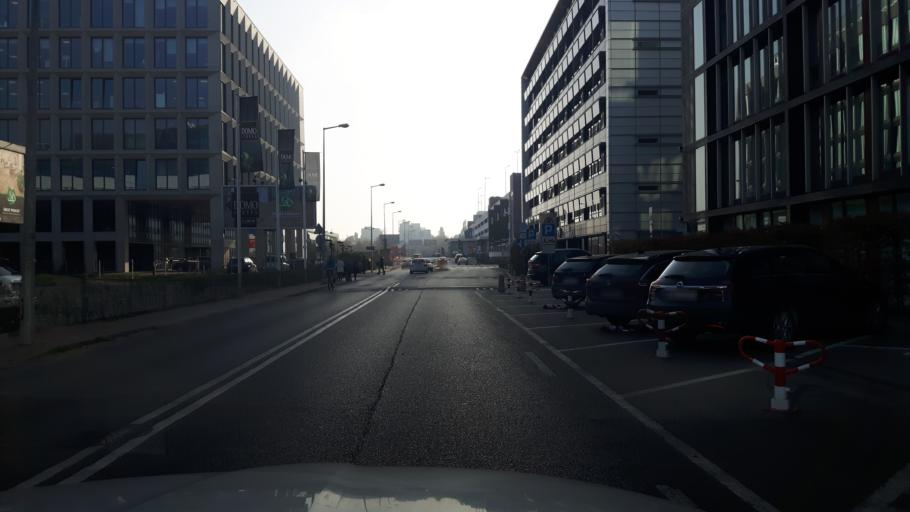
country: PL
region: Masovian Voivodeship
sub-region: Warszawa
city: Mokotow
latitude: 52.1820
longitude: 21.0060
